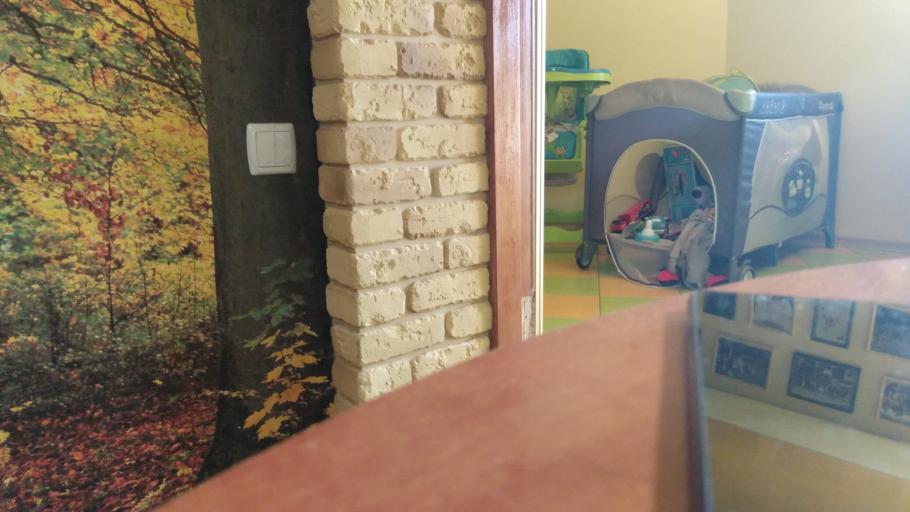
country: RU
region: Tverskaya
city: Bologoye
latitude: 57.9160
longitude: 34.2270
